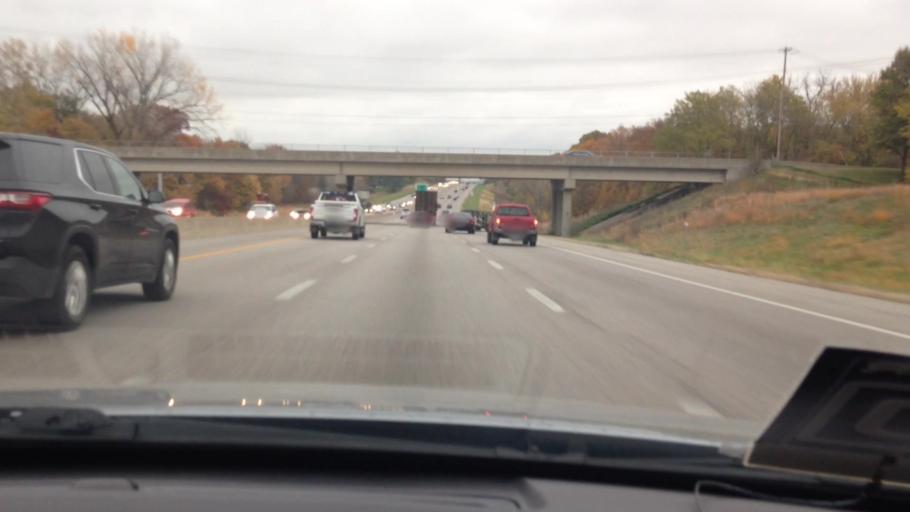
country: US
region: Kansas
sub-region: Johnson County
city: Shawnee
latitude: 39.1059
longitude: -94.7298
